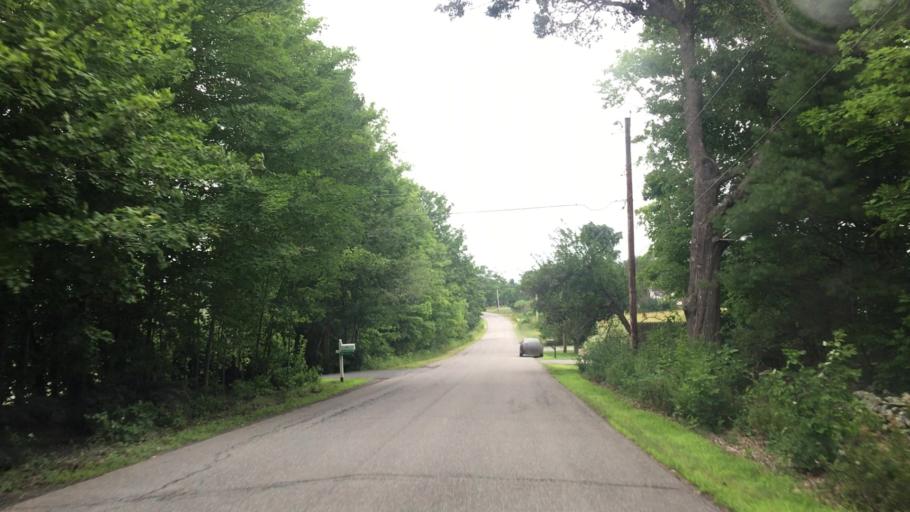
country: US
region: Maine
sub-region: Penobscot County
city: Veazie
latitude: 44.8521
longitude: -68.7444
